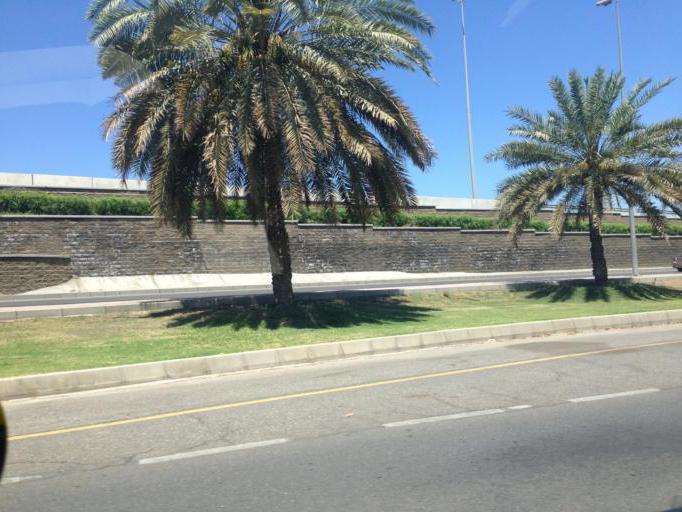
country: OM
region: Muhafazat Masqat
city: As Sib al Jadidah
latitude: 23.6536
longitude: 58.2077
